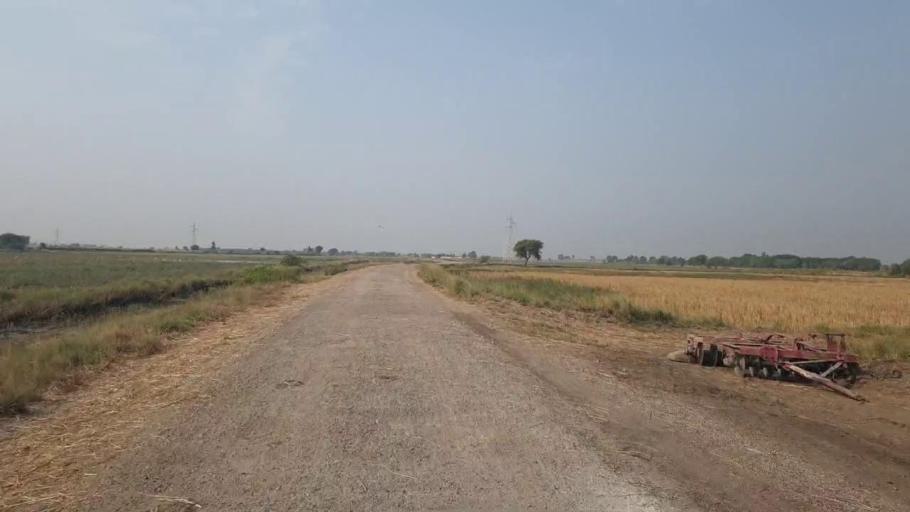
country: PK
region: Sindh
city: Tando Muhammad Khan
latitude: 25.1091
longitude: 68.5137
